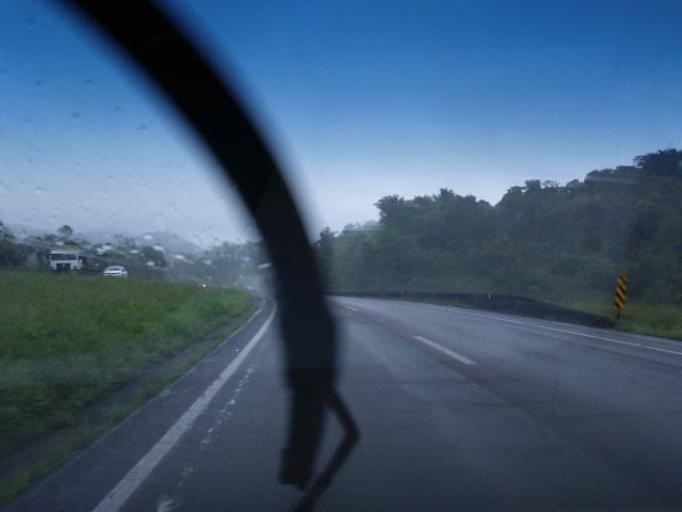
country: BR
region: Parana
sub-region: Antonina
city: Antonina
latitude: -25.0899
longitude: -48.6462
